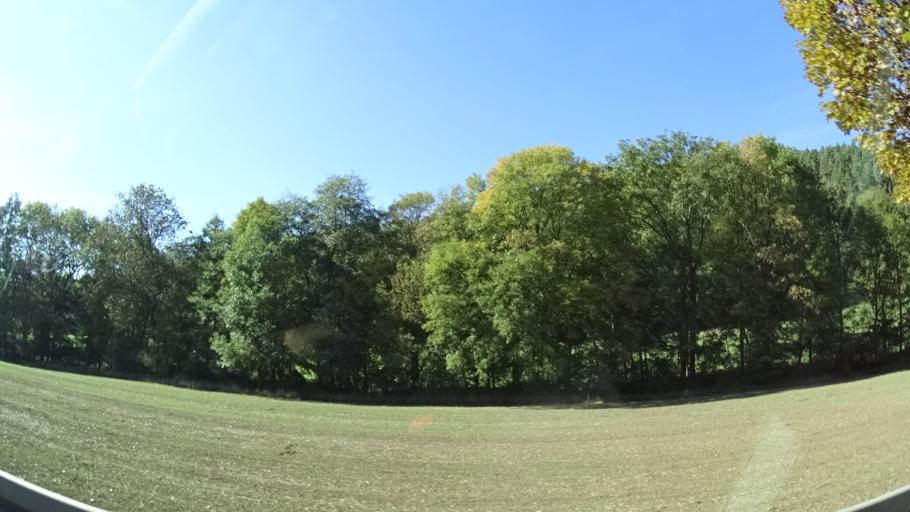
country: DE
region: Thuringia
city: Rudolstadt
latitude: 50.7617
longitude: 11.3103
